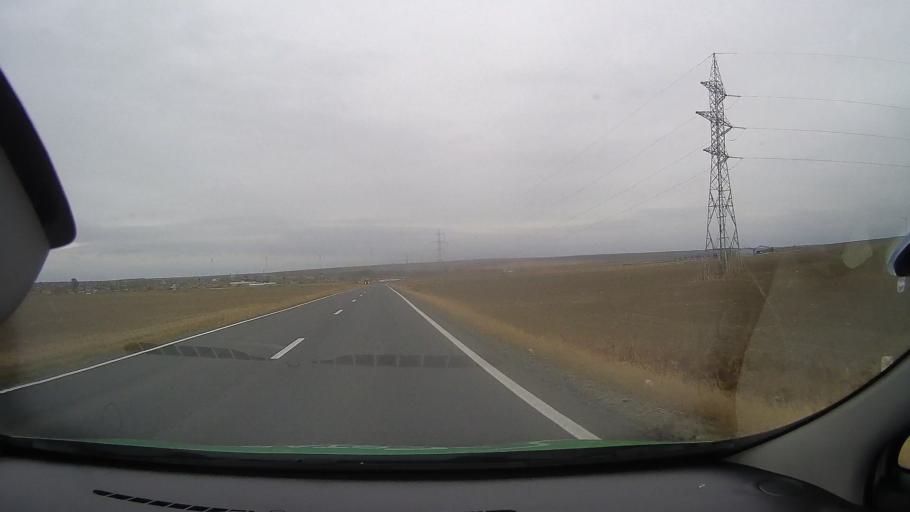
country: RO
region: Constanta
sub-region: Comuna Nicolae Balcescu
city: Dorobantu
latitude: 44.4181
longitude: 28.3141
